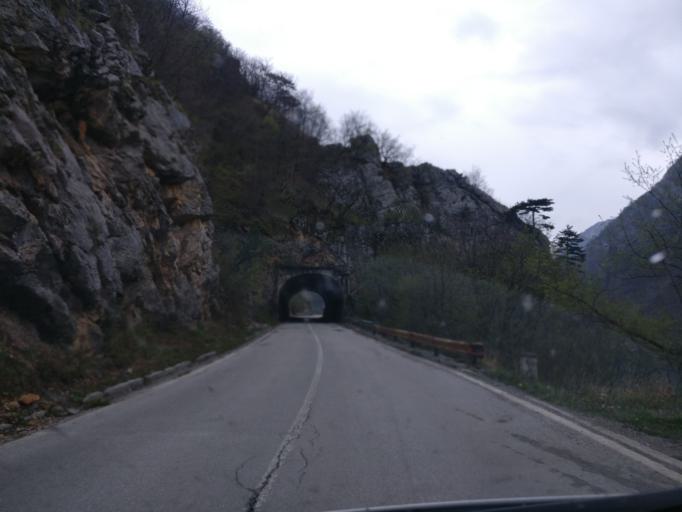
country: ME
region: Opstina Pluzine
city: Pluzine
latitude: 43.2455
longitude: 18.8345
